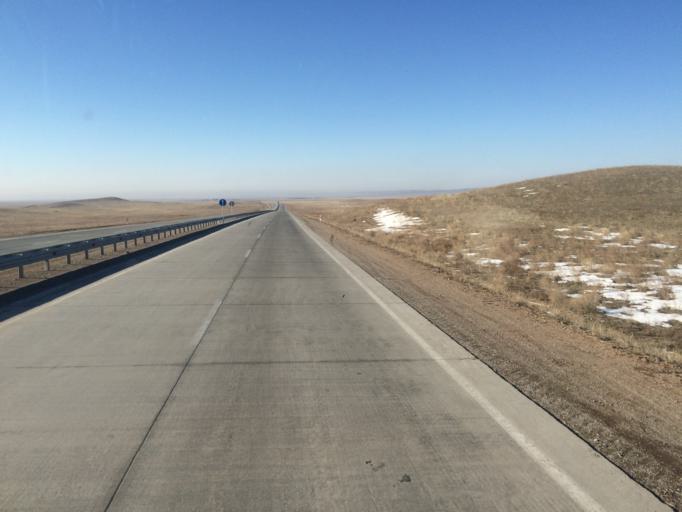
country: KZ
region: Zhambyl
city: Georgiyevka
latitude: 43.3395
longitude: 74.4614
